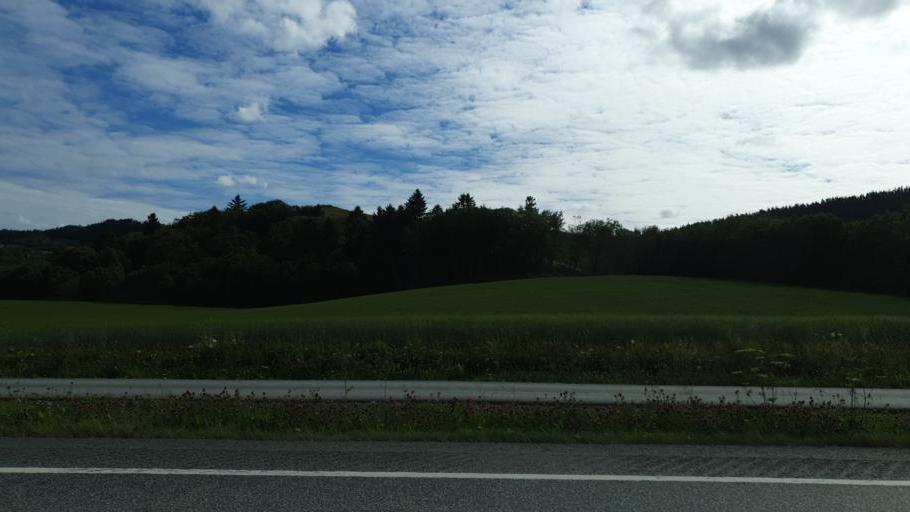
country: NO
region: Sor-Trondelag
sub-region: Melhus
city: Lundamo
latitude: 63.1765
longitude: 10.3168
